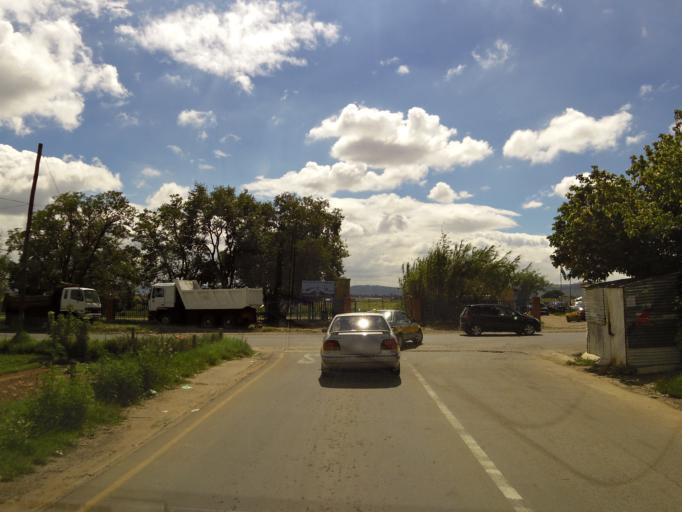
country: LS
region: Maseru
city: Maseru
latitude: -29.3094
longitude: 27.4989
